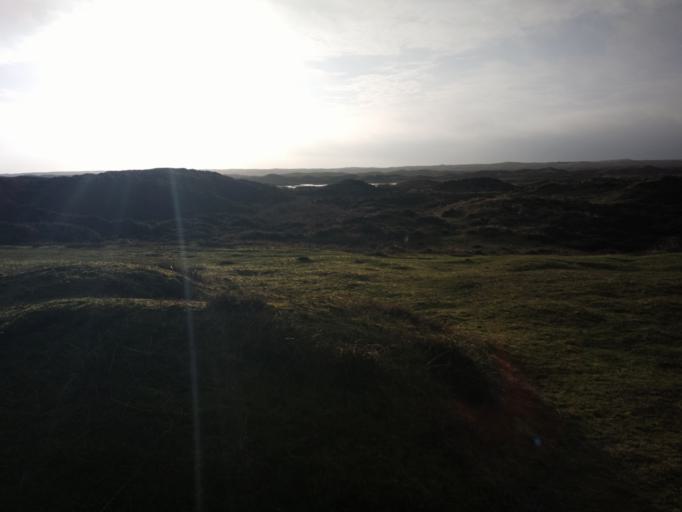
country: NL
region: North Holland
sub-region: Gemeente Texel
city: Den Burg
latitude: 53.0314
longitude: 4.7271
